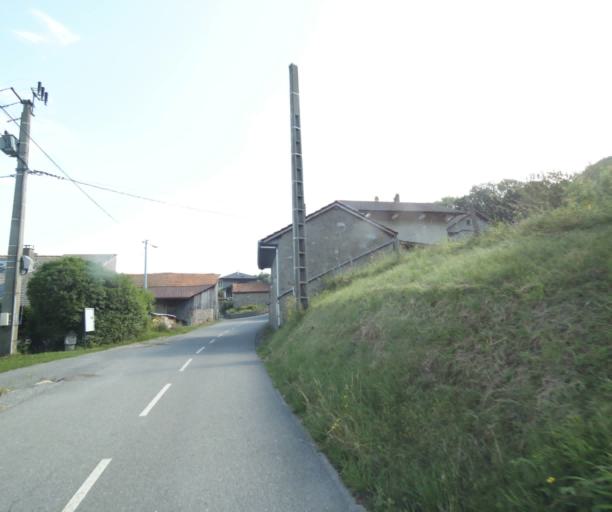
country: FR
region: Rhone-Alpes
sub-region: Departement de la Haute-Savoie
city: Lyaud
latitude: 46.3152
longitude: 6.5102
